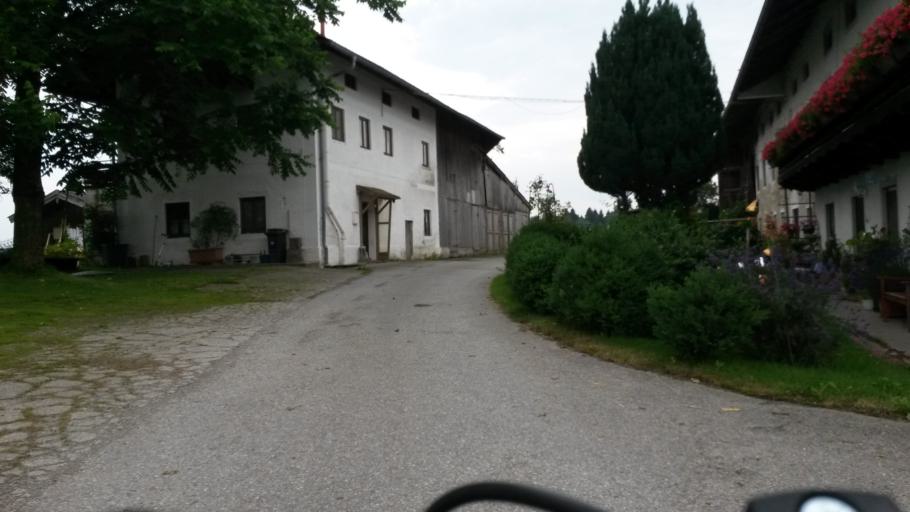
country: DE
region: Bavaria
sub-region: Upper Bavaria
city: Hoslwang
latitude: 47.9394
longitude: 12.3398
